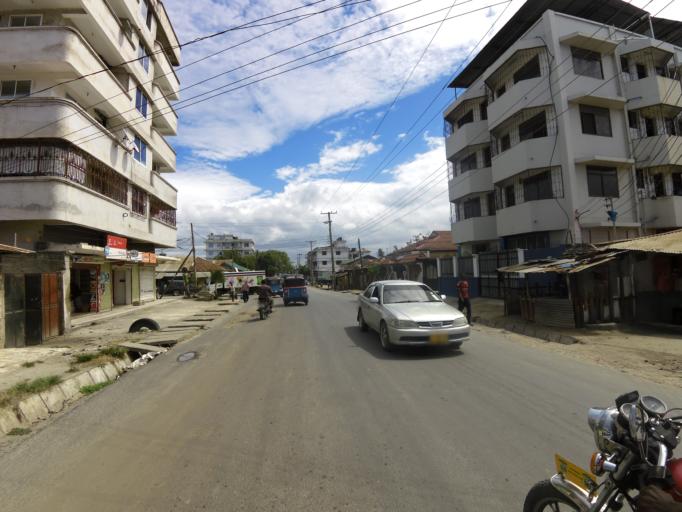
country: TZ
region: Dar es Salaam
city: Magomeni
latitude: -6.8013
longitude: 39.2465
